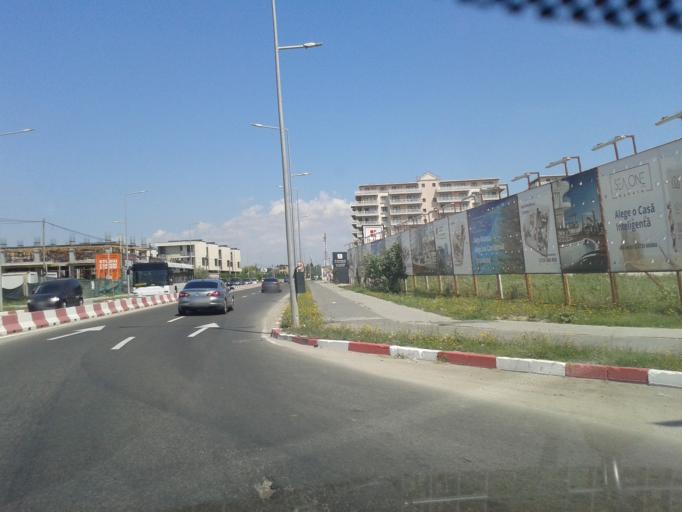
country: RO
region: Constanta
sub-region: Comuna Navodari
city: Navodari
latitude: 44.2764
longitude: 28.6176
